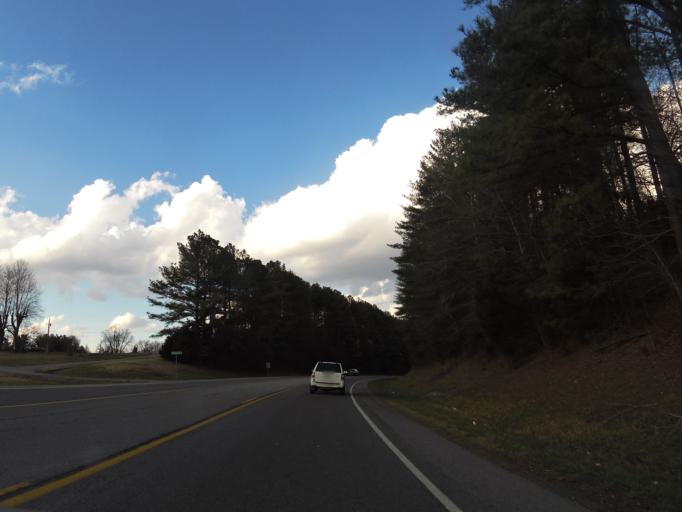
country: US
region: Tennessee
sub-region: Smith County
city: Gordonsville
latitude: 36.1961
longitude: -85.9560
